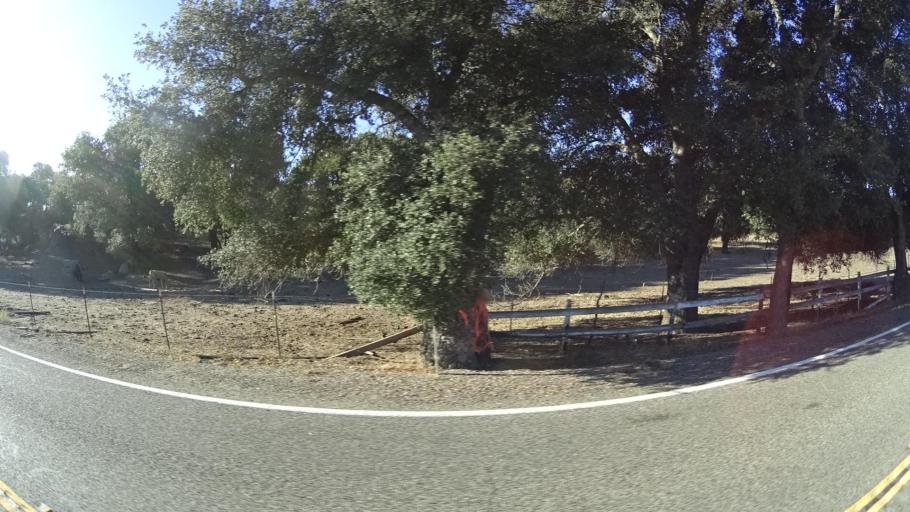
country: MX
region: Baja California
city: Tecate
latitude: 32.5998
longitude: -116.5861
